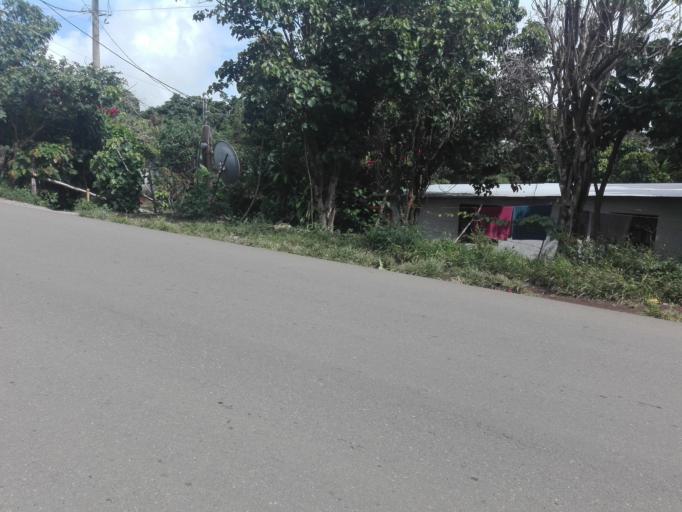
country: GT
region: Escuintla
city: San Vicente Pacaya
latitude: 14.3686
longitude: -90.5623
